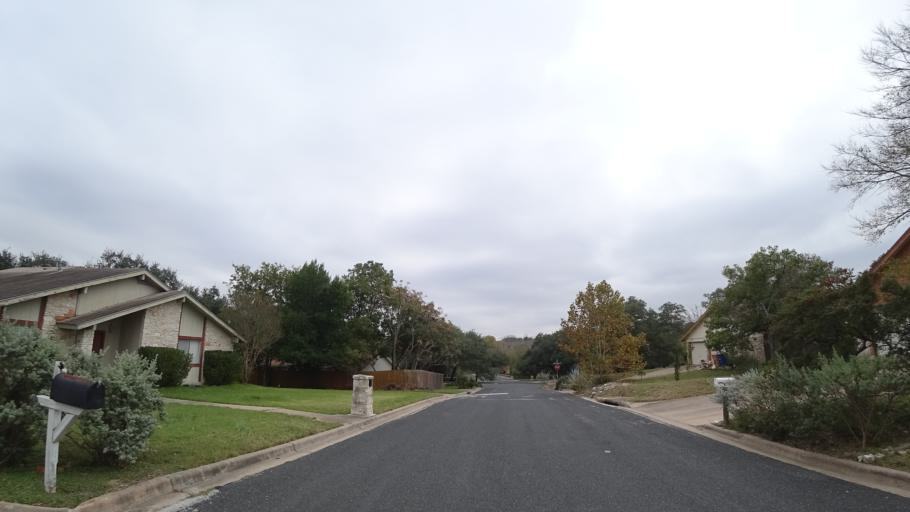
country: US
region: Texas
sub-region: Travis County
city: Barton Creek
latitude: 30.2390
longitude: -97.8889
